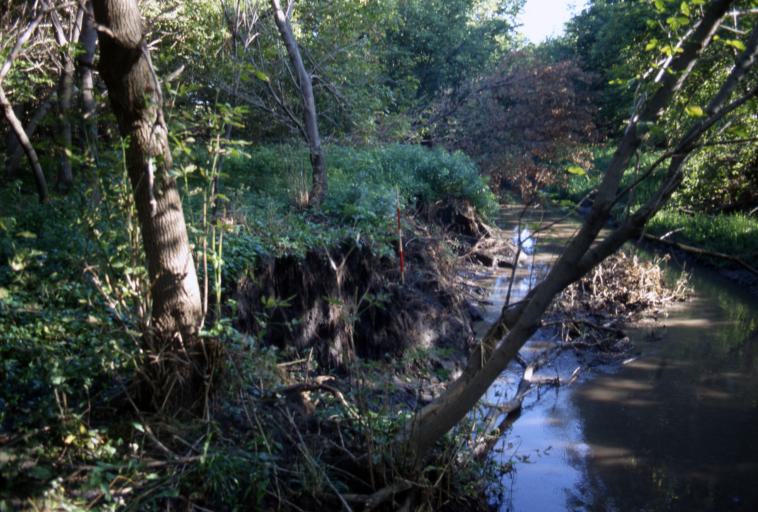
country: US
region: Minnesota
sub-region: Wabasha County
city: Elgin
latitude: 44.1084
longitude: -92.2590
